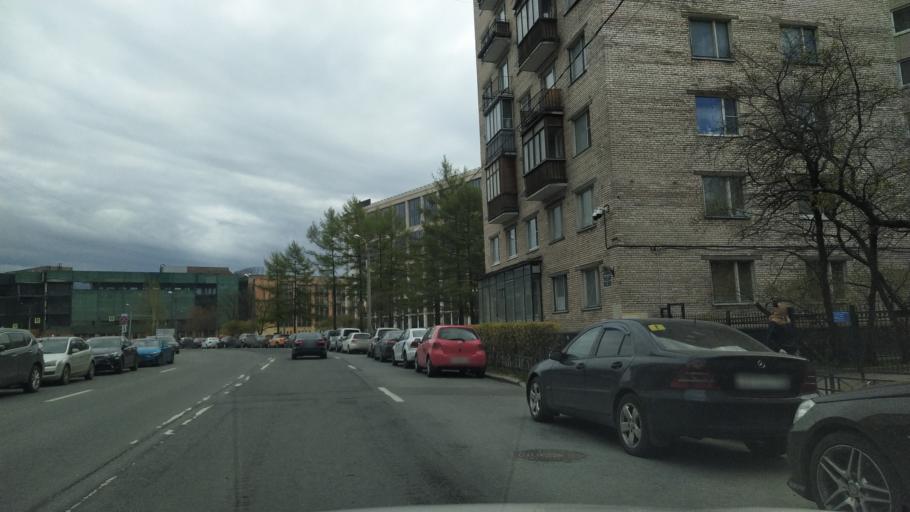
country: RU
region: St.-Petersburg
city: Centralniy
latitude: 59.9402
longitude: 30.3855
